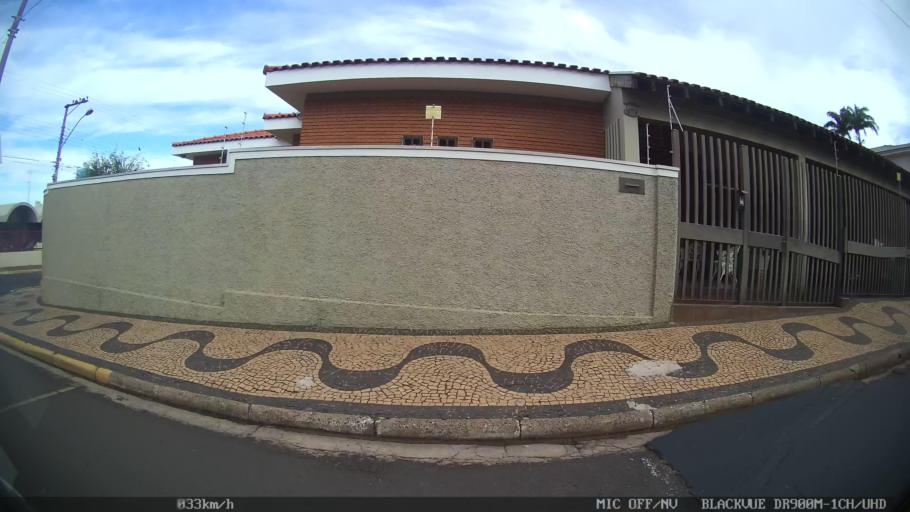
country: BR
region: Sao Paulo
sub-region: Catanduva
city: Catanduva
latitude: -21.1260
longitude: -48.9666
